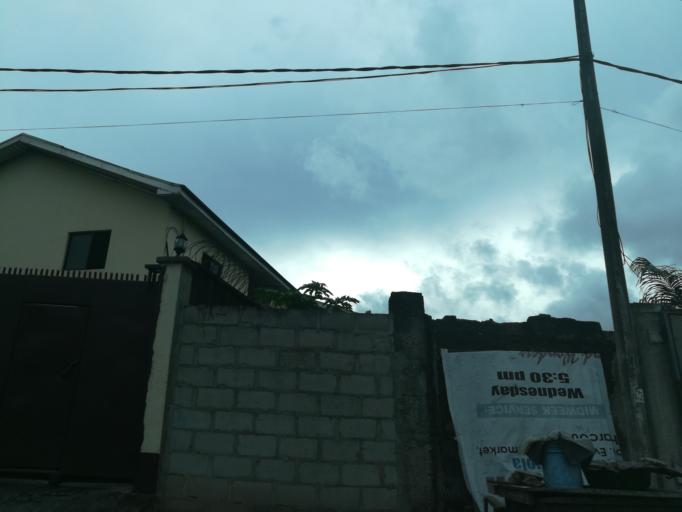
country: NG
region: Rivers
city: Port Harcourt
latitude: 4.8166
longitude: 6.9901
